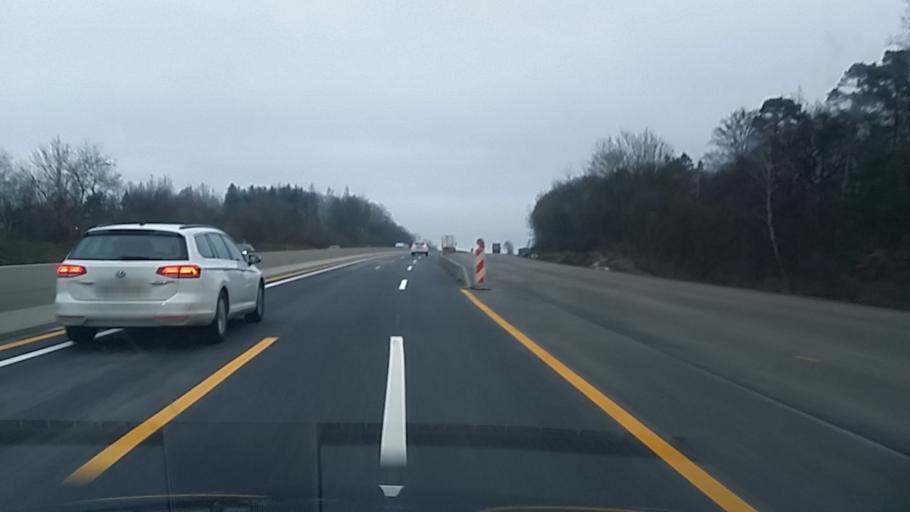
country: DE
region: Hesse
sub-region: Regierungsbezirk Kassel
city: Guxhagen
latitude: 51.1759
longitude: 9.4728
